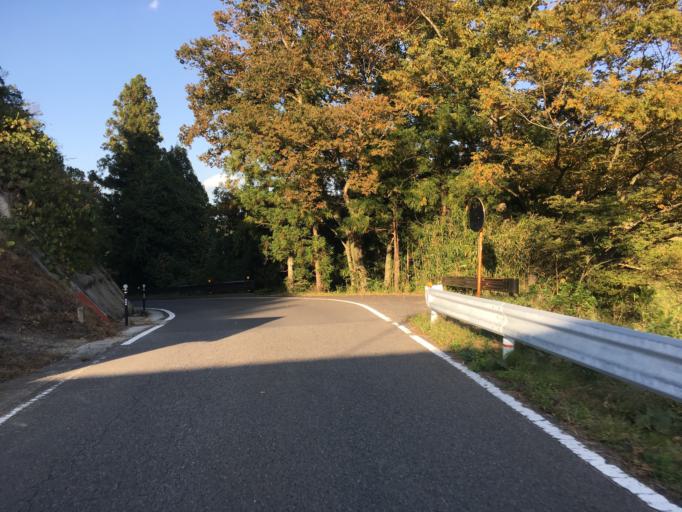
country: JP
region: Fukushima
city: Nihommatsu
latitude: 37.6335
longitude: 140.5660
